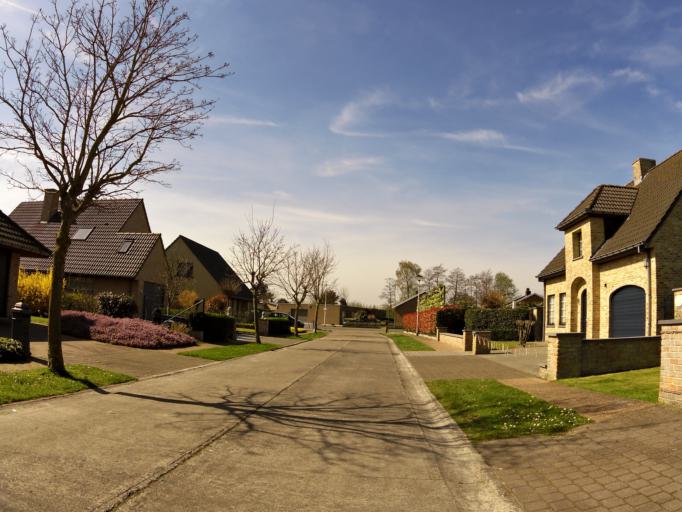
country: BE
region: Flanders
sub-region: Provincie West-Vlaanderen
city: Oudenburg
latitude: 51.1882
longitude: 3.0026
